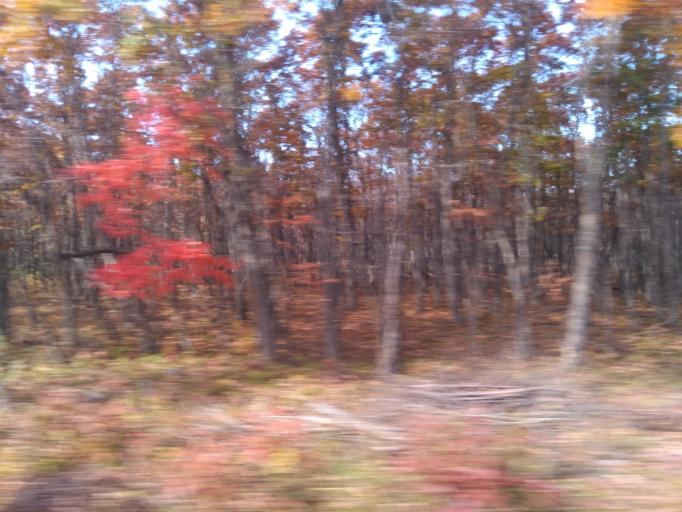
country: JP
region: Hokkaido
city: Tomakomai
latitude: 42.6920
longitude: 141.7306
